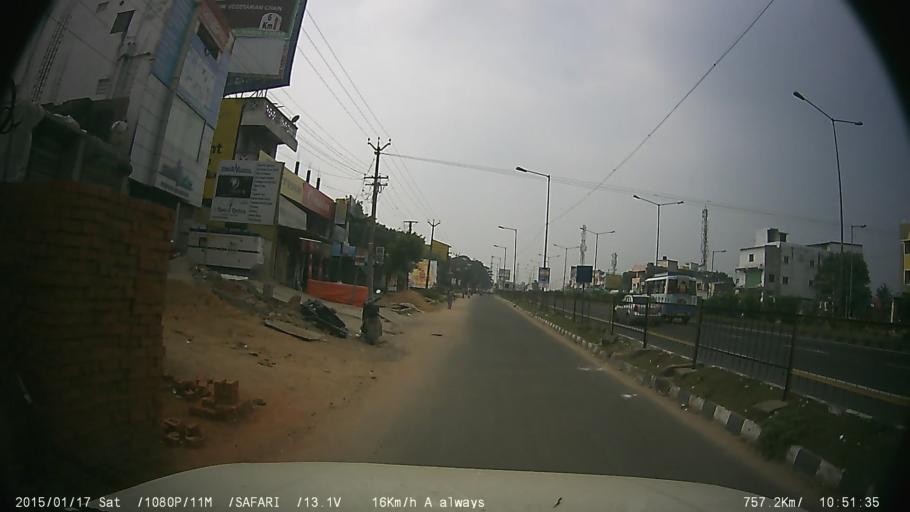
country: IN
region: Tamil Nadu
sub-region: Kancheepuram
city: Guduvancheri
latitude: 12.8478
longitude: 80.0634
